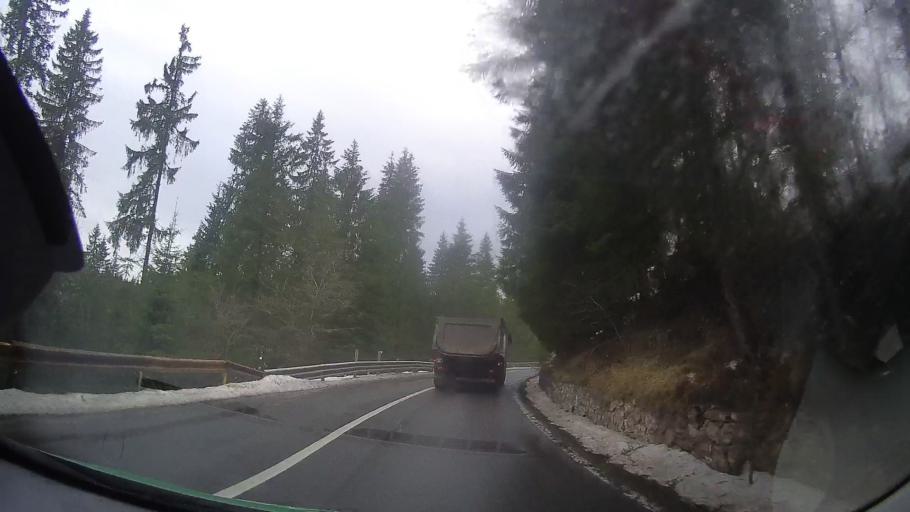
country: RO
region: Harghita
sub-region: Municipiul Gheorgheni
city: Gheorgheni
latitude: 46.7784
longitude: 25.7261
